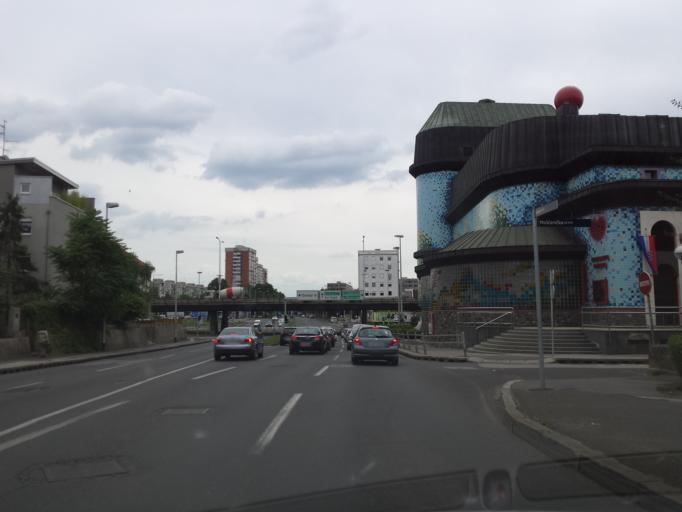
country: HR
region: Grad Zagreb
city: Zagreb - Centar
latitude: 45.7951
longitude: 15.9439
